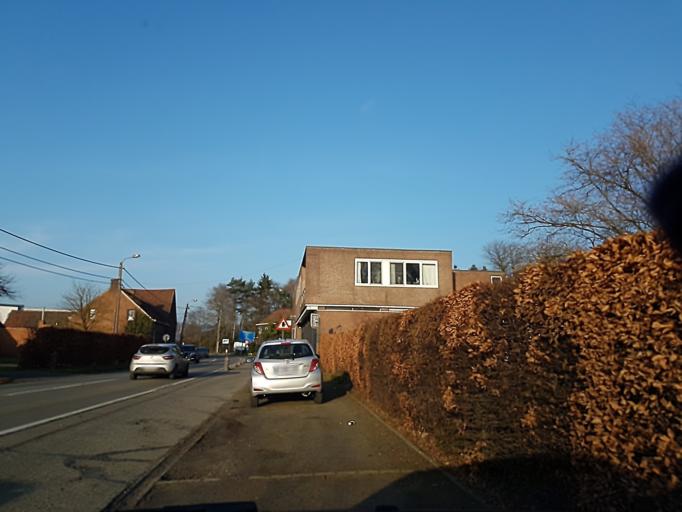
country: BE
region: Flanders
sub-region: Provincie Antwerpen
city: Heist-op-den-Berg
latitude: 51.0659
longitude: 4.7365
